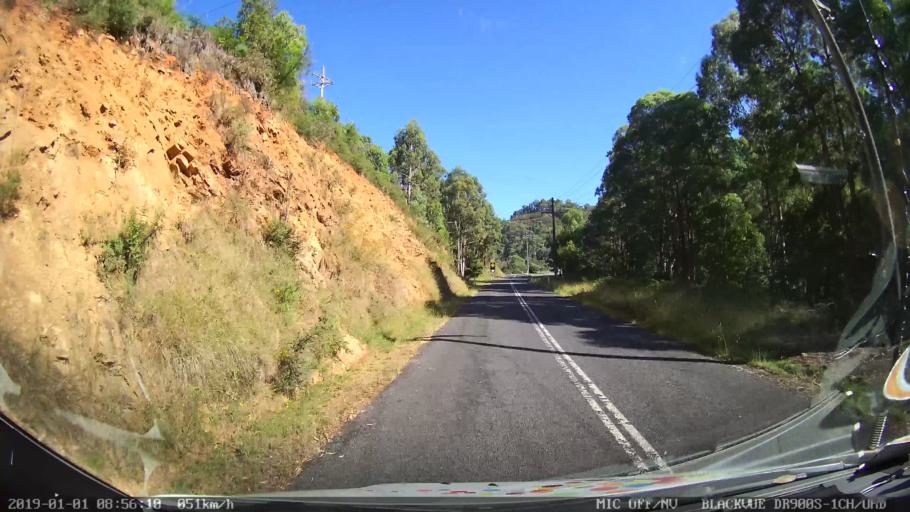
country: AU
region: New South Wales
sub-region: Snowy River
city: Jindabyne
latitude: -36.2485
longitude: 148.1891
